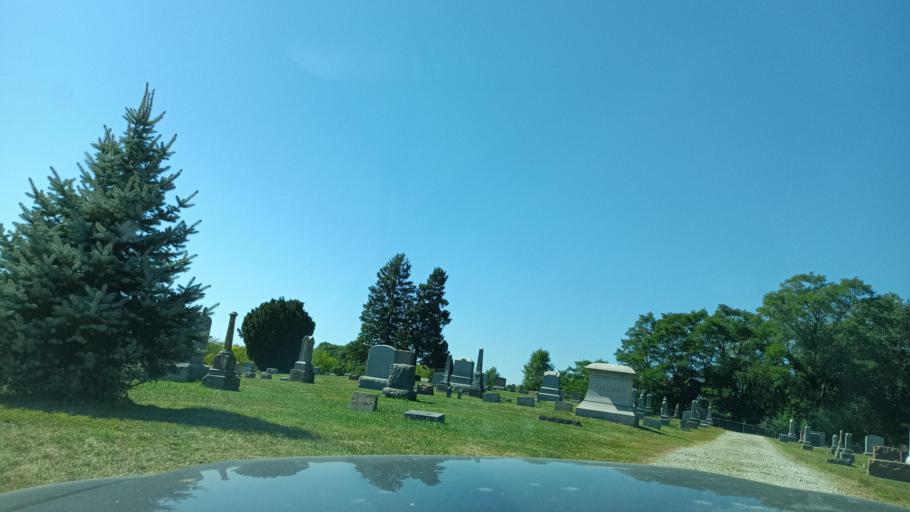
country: US
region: Illinois
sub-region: McLean County
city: Danvers
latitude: 40.5953
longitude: -89.2028
